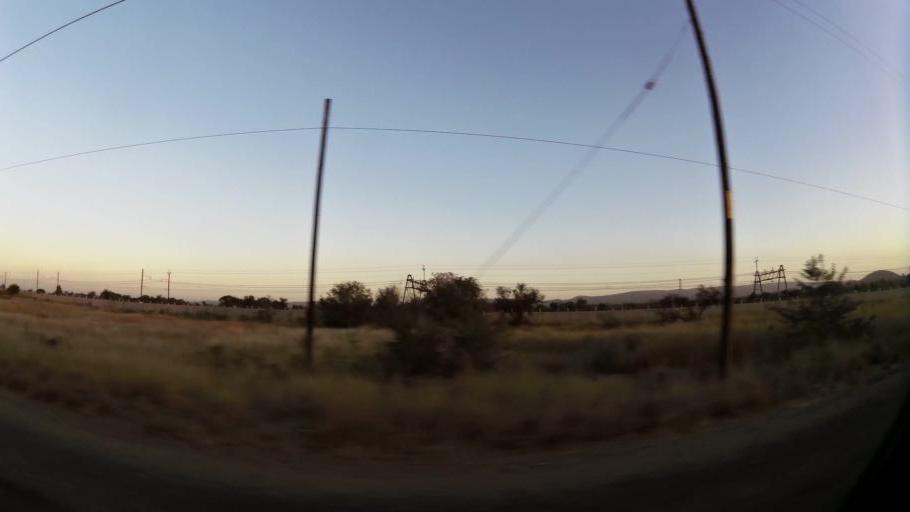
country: ZA
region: North-West
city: Ga-Rankuwa
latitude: -25.6220
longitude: 28.0273
